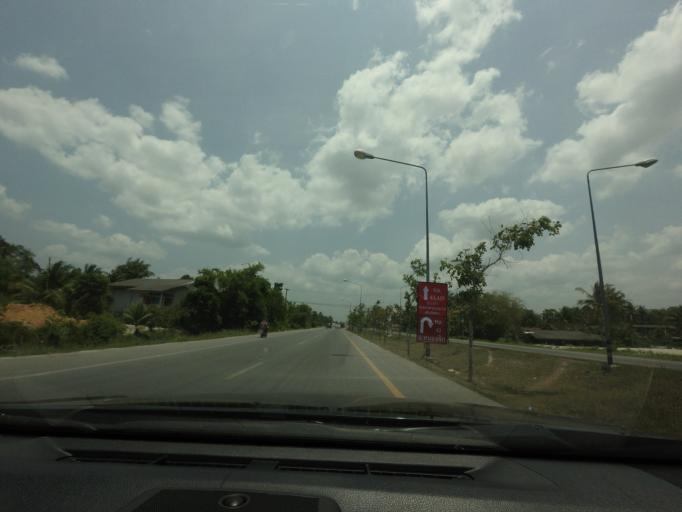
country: TH
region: Pattani
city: Pattani
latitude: 6.8513
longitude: 101.2235
